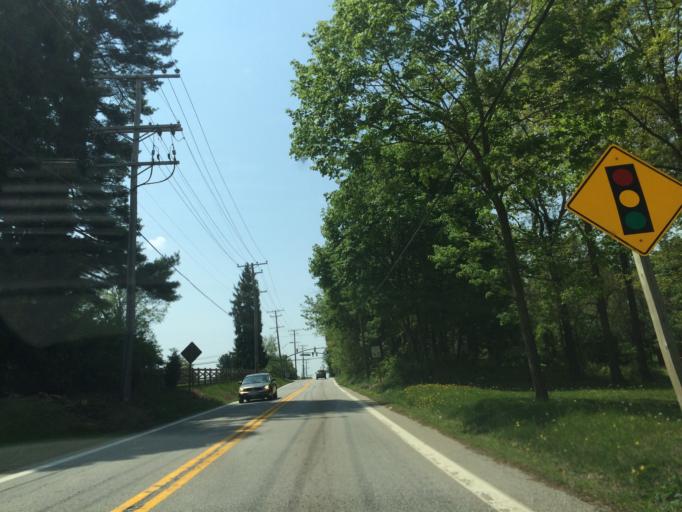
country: US
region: Maryland
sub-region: Carroll County
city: Sykesville
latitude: 39.3372
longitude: -77.0136
